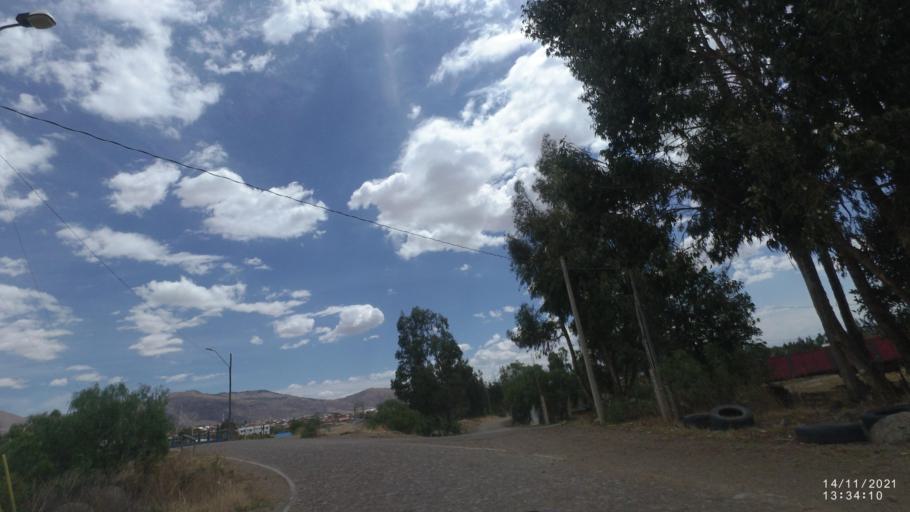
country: BO
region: Cochabamba
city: Colomi
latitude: -17.4012
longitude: -65.9840
